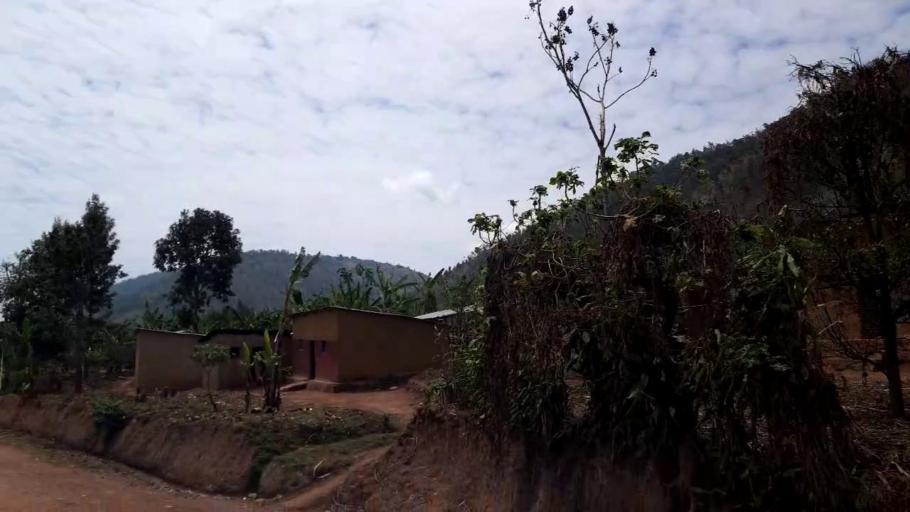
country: RW
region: Northern Province
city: Byumba
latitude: -1.5020
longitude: 30.1928
